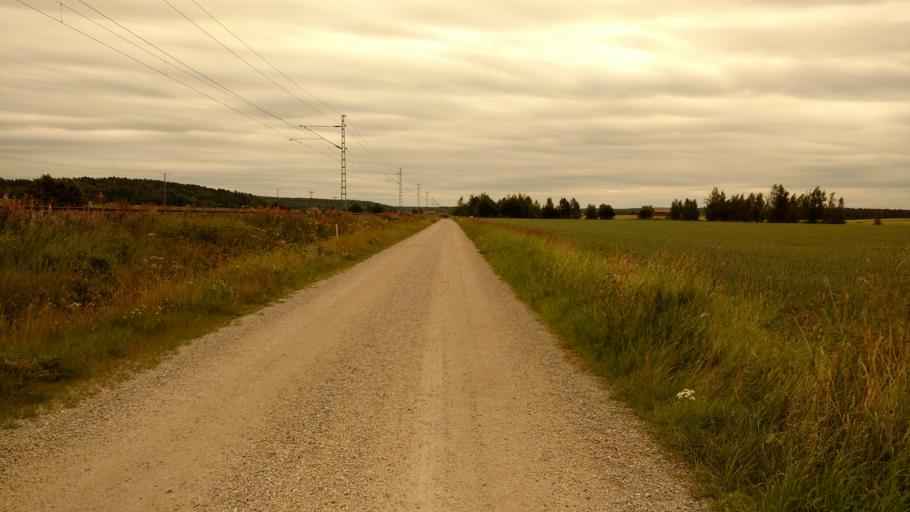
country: FI
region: Varsinais-Suomi
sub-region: Turku
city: Paimio
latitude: 60.4207
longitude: 22.8296
